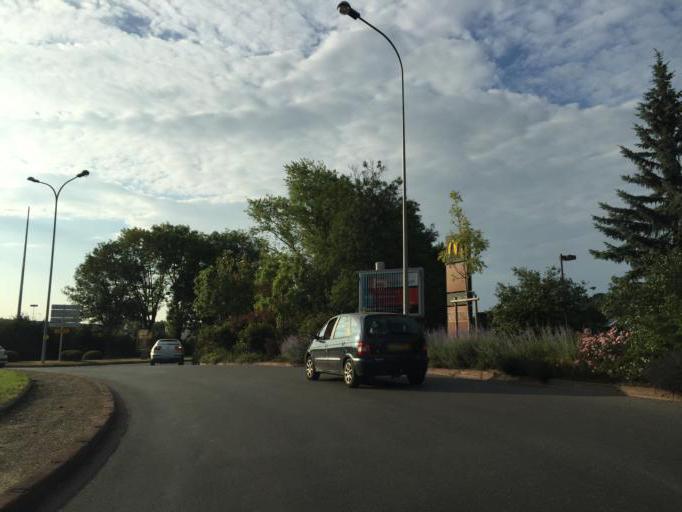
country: FR
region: Auvergne
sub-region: Departement de l'Allier
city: Vichy
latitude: 46.1421
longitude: 3.4155
